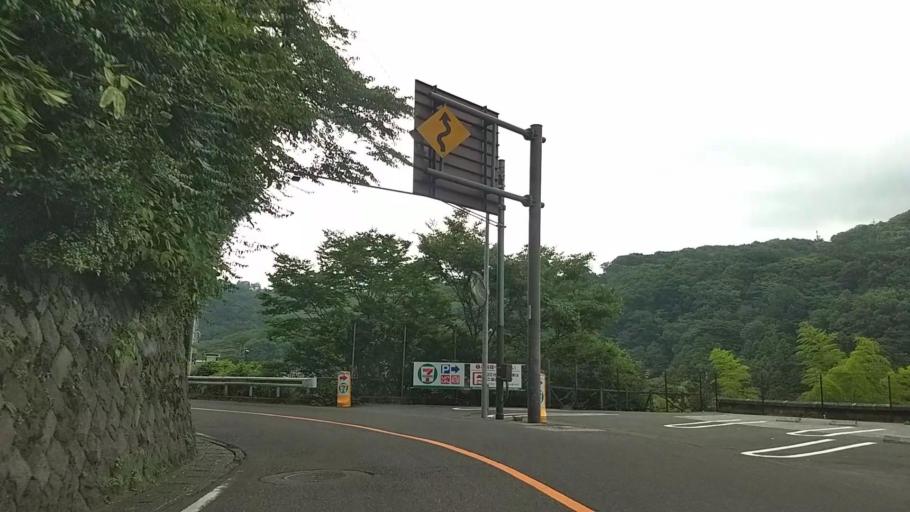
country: JP
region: Kanagawa
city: Hakone
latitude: 35.2453
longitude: 139.0587
